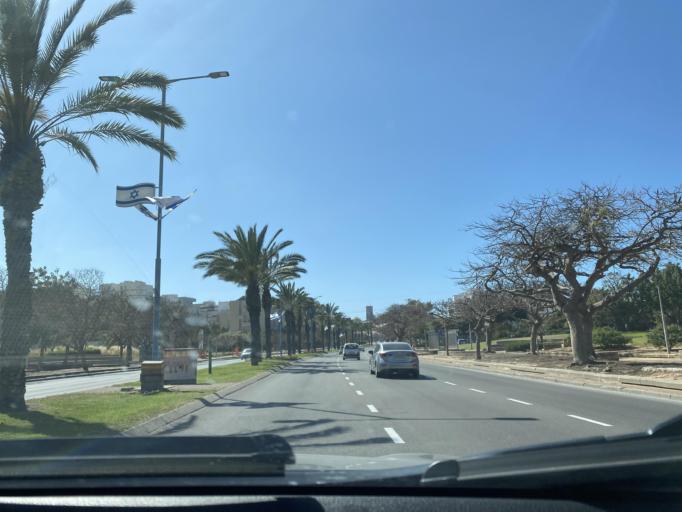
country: IL
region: Southern District
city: Ashqelon
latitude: 31.6742
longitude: 34.5807
